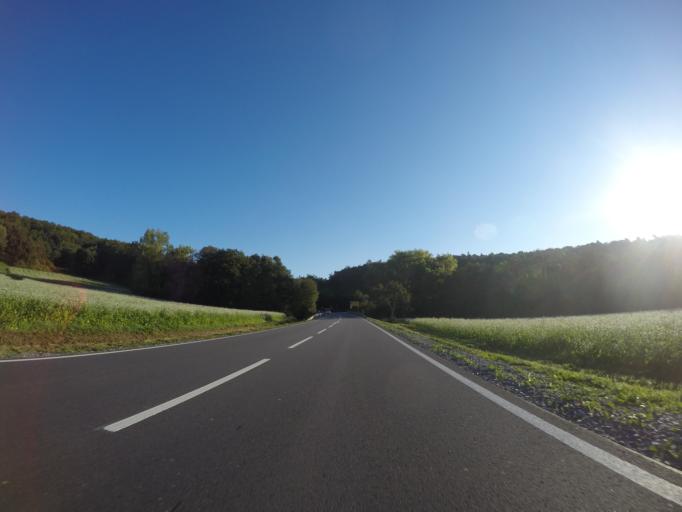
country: DE
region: Bavaria
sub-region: Regierungsbezirk Unterfranken
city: Kreuzwertheim
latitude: 49.7814
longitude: 9.5429
